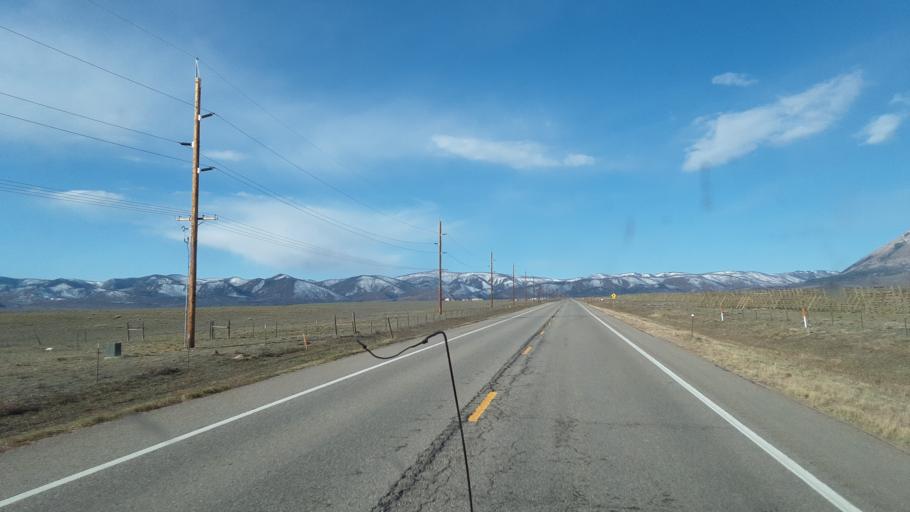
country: US
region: Colorado
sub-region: Huerfano County
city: Walsenburg
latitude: 37.5440
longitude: -105.0144
